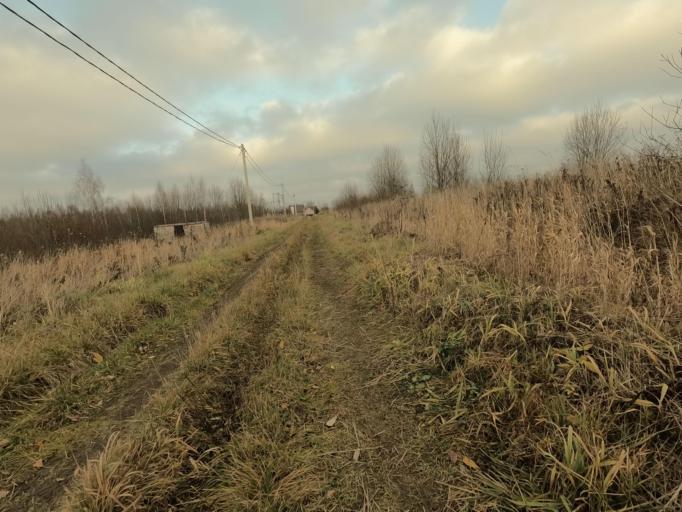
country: RU
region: Leningrad
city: Mga
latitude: 59.7538
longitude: 31.0721
